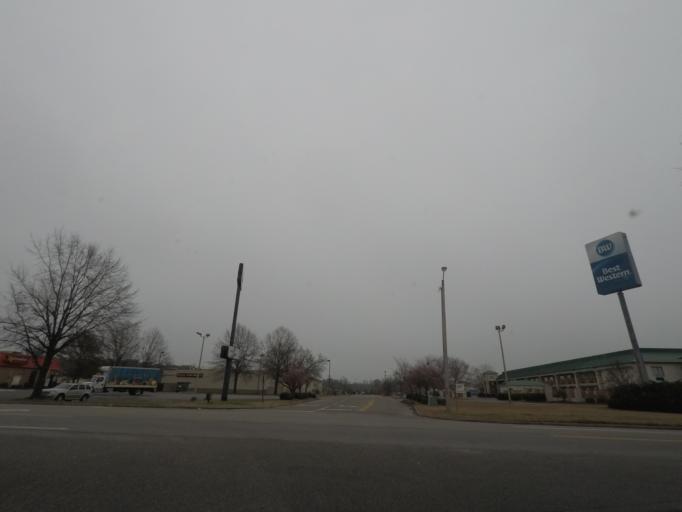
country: US
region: North Carolina
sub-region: Robeson County
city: Lumberton
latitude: 34.6672
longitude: -79.0048
